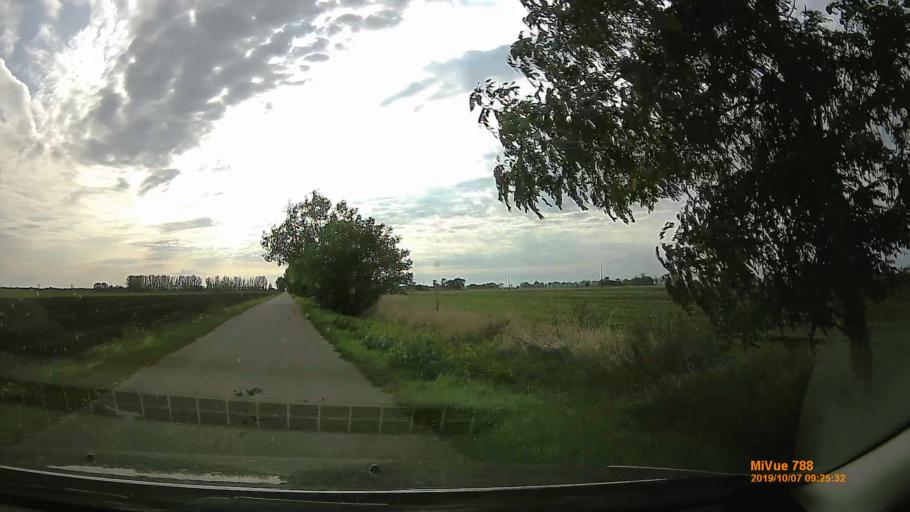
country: HU
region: Bekes
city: Szarvas
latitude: 46.8124
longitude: 20.6523
